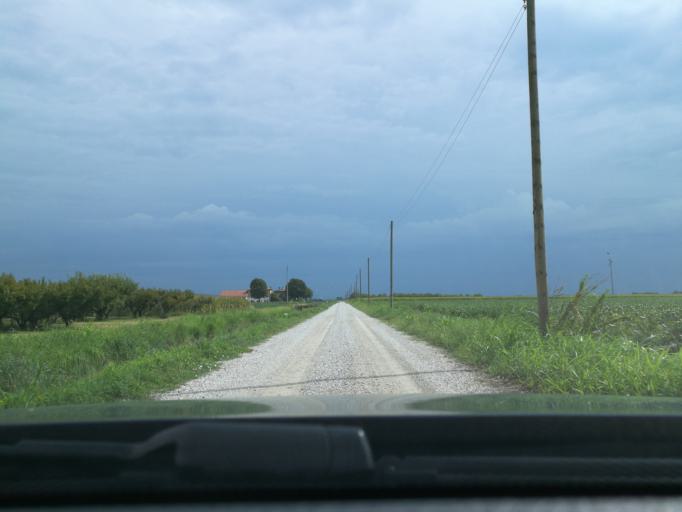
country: IT
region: Friuli Venezia Giulia
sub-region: Provincia di Udine
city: Pertegada
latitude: 45.7096
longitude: 13.0598
